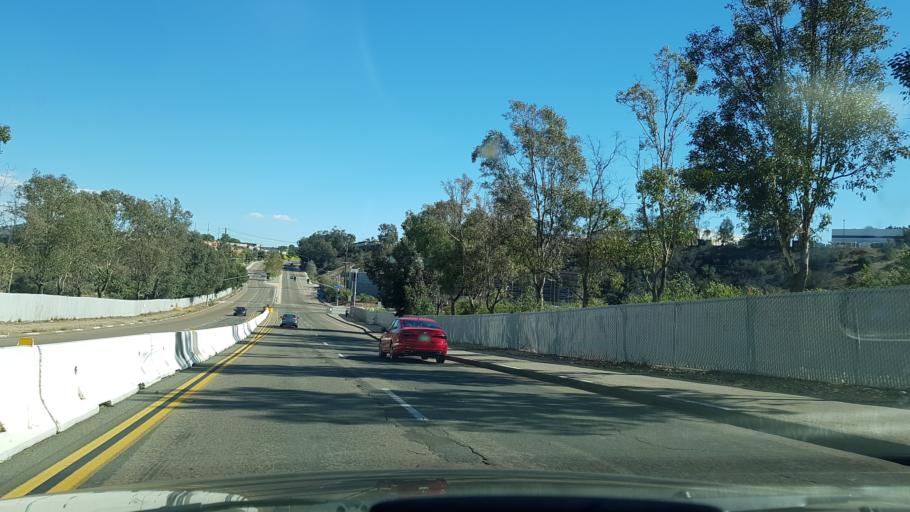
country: US
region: California
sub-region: San Diego County
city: Fairbanks Ranch
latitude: 32.8994
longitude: -117.1422
